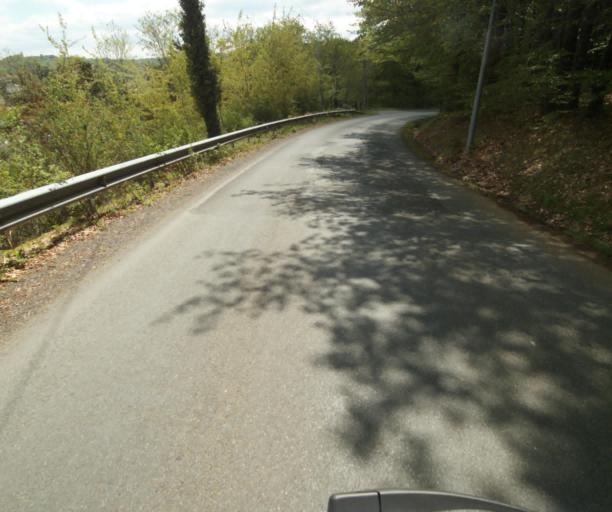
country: FR
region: Limousin
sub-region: Departement de la Correze
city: Tulle
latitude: 45.2842
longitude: 1.7665
